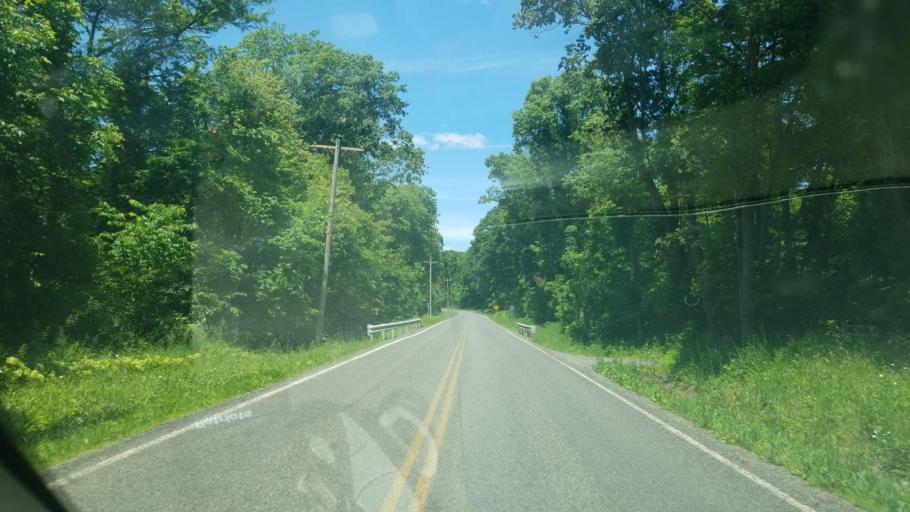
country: US
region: Ohio
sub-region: Columbiana County
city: Glenmoor
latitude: 40.7387
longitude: -80.6420
